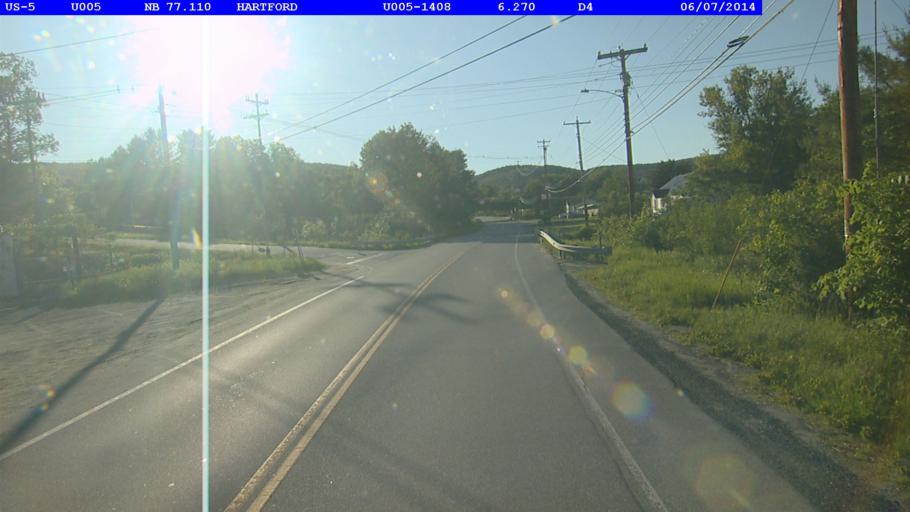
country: US
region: Vermont
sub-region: Windsor County
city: Wilder
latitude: 43.6809
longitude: -72.3130
